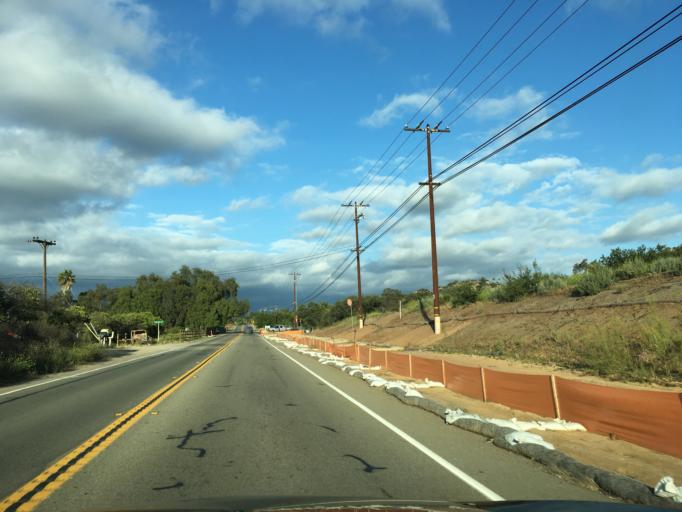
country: US
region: California
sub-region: San Diego County
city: Hidden Meadows
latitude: 33.2563
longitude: -117.0835
